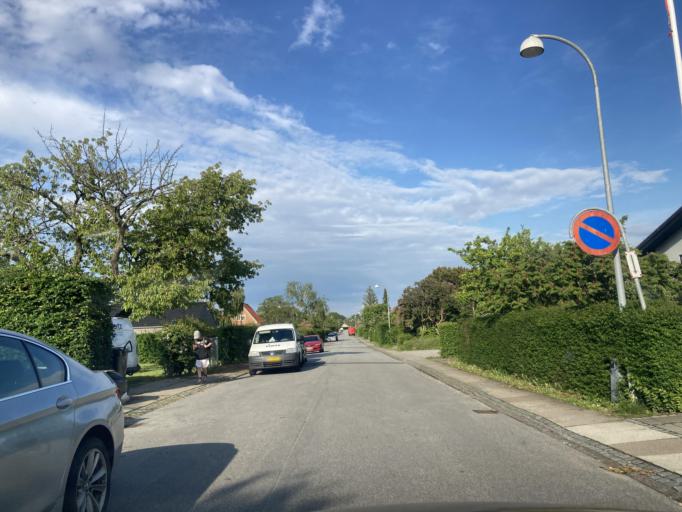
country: DK
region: Capital Region
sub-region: Hvidovre Kommune
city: Hvidovre
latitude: 55.6399
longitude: 12.4803
